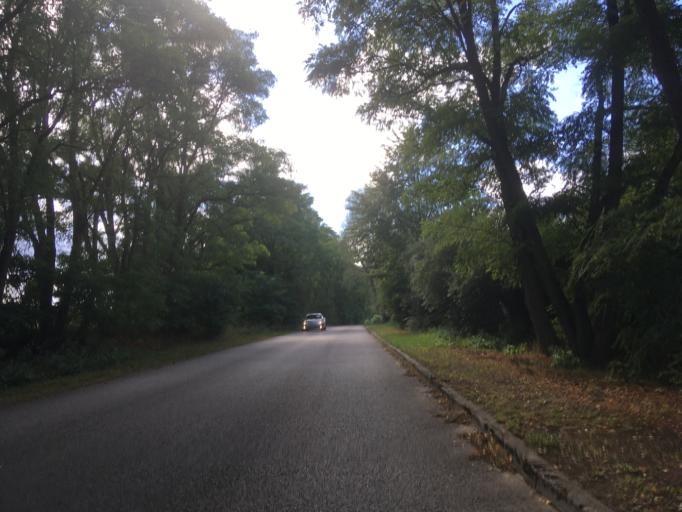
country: DE
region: Brandenburg
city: Oderberg
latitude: 52.9218
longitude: 14.0305
